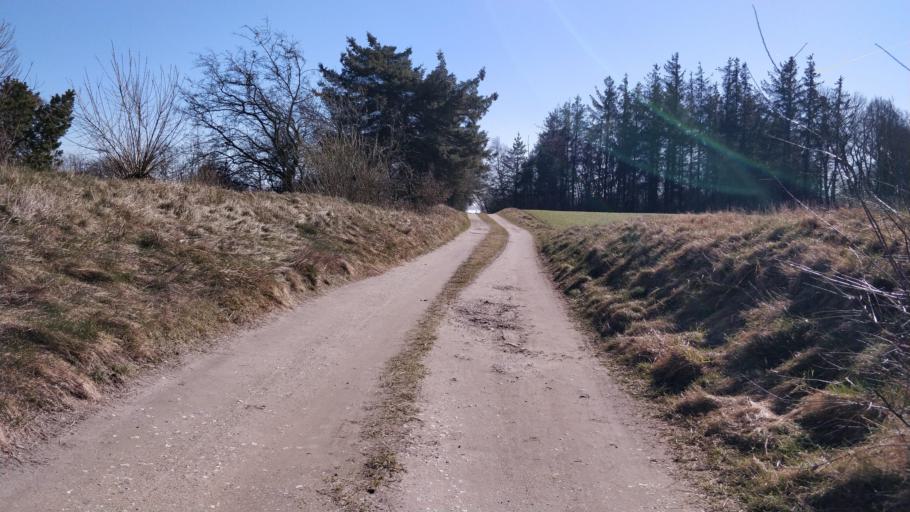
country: DK
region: North Denmark
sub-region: Jammerbugt Kommune
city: Abybro
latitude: 57.0703
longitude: 9.7443
